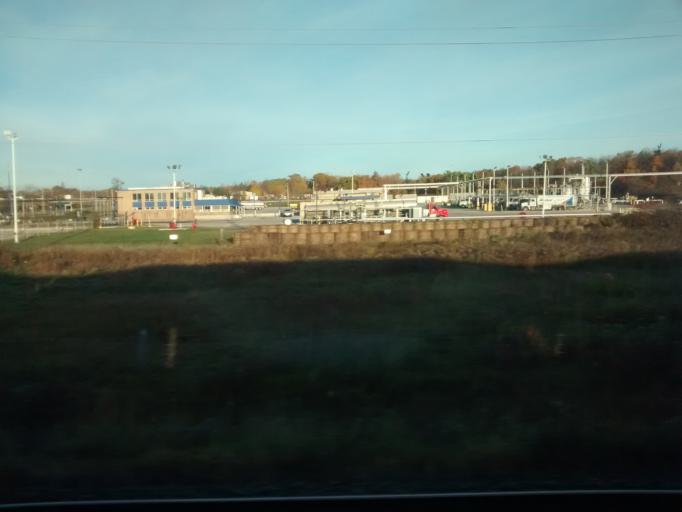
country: CA
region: Ontario
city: Oakville
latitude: 43.4000
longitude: -79.7397
